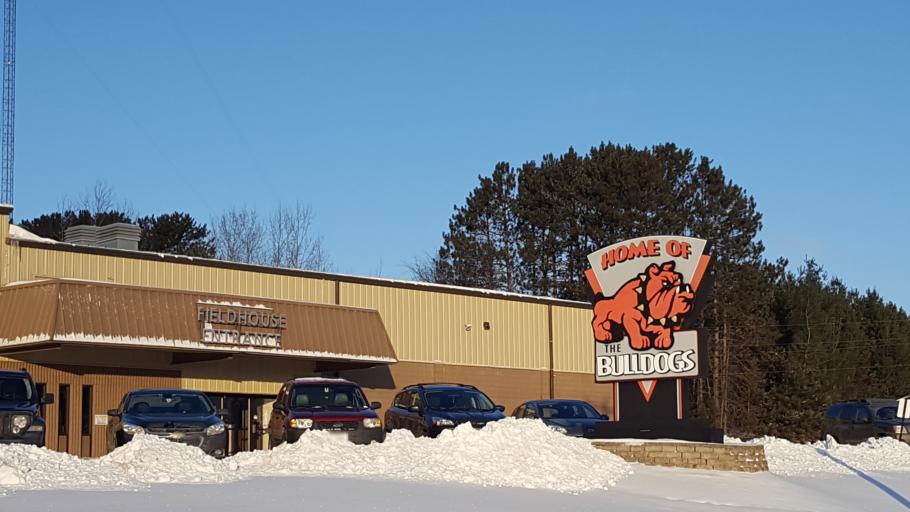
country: US
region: Wisconsin
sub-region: Clark County
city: Neillsville
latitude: 44.5922
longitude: -90.4622
